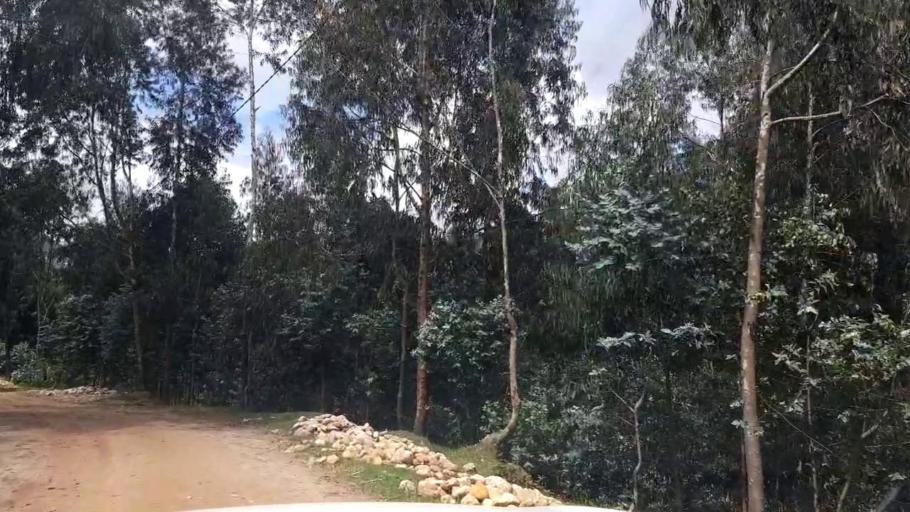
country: RW
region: Western Province
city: Kibuye
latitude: -1.9099
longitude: 29.4574
